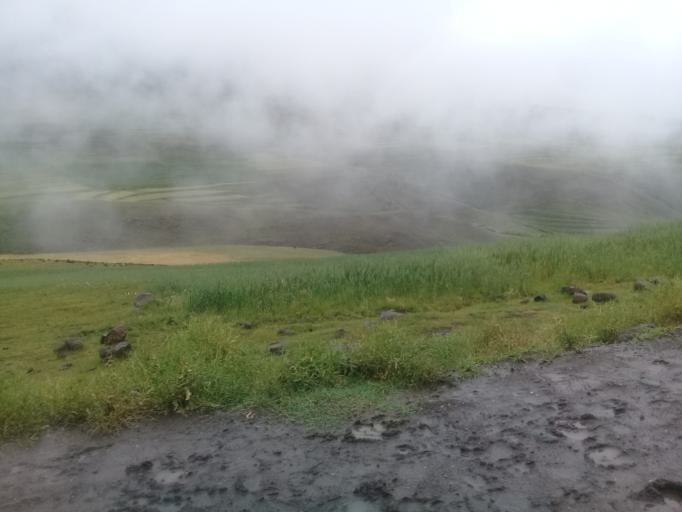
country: LS
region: Mokhotlong
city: Mokhotlong
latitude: -29.3813
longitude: 28.9815
